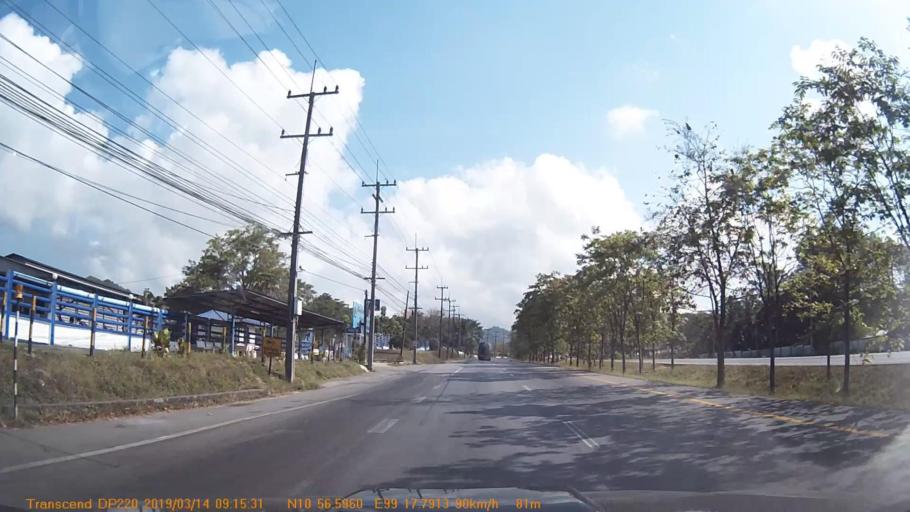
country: TH
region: Prachuap Khiri Khan
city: Bang Saphan Noi
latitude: 10.9440
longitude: 99.2969
